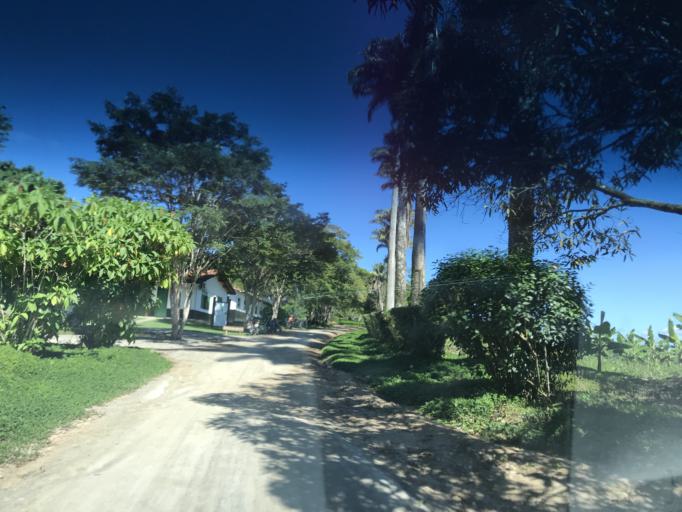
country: BR
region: Bahia
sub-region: Mutuipe
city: Mutuipe
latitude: -13.3726
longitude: -39.3715
